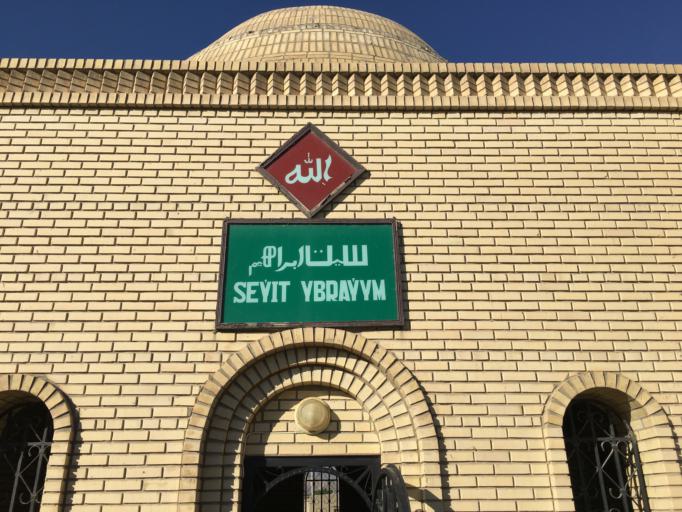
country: TM
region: Ahal
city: Baharly
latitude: 38.3712
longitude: 57.5022
